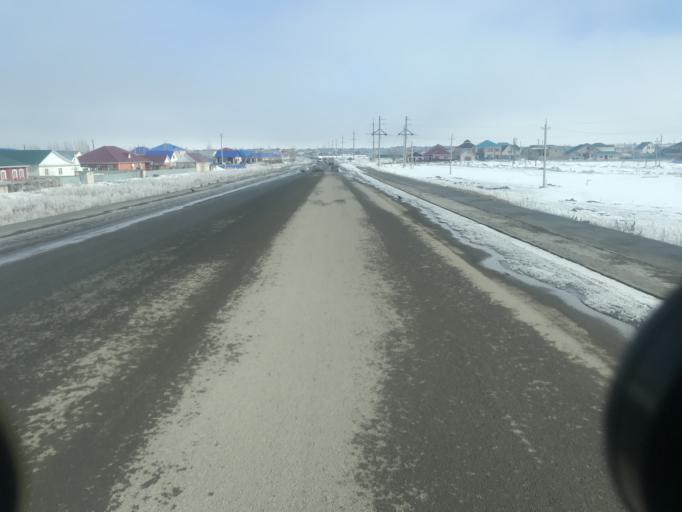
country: KZ
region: Aqtoebe
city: Aqtobe
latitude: 50.2756
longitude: 57.2687
